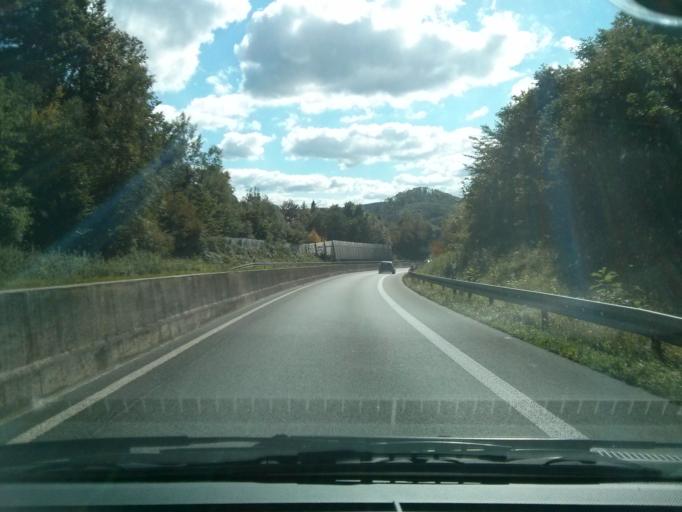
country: DE
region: North Rhine-Westphalia
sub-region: Regierungsbezirk Arnsberg
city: Arnsberg
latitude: 51.4146
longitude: 8.0552
